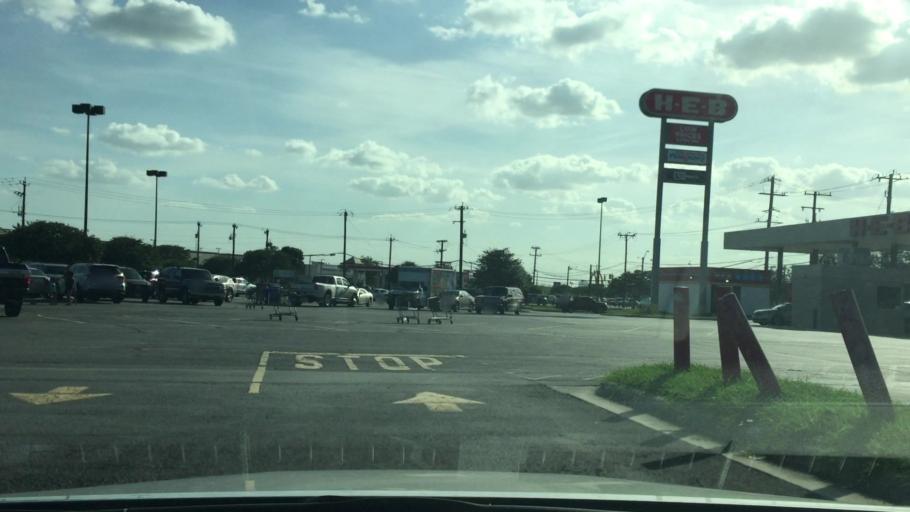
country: US
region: Texas
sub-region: Bexar County
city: Kirby
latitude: 29.4805
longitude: -98.3591
